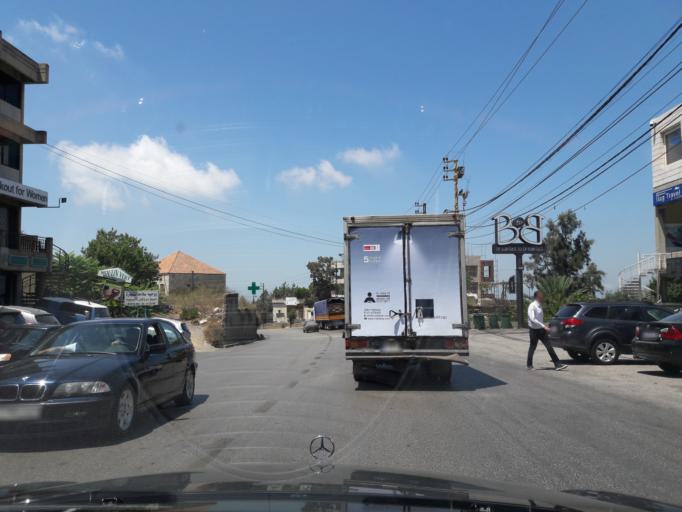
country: LB
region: Mont-Liban
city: Djounie
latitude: 33.9213
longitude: 35.6332
